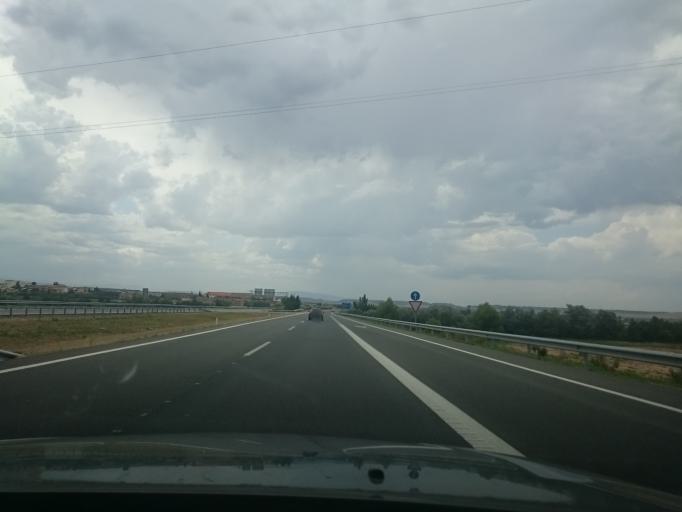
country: ES
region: Navarre
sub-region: Provincia de Navarra
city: Murchante
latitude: 42.0324
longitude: -1.6360
